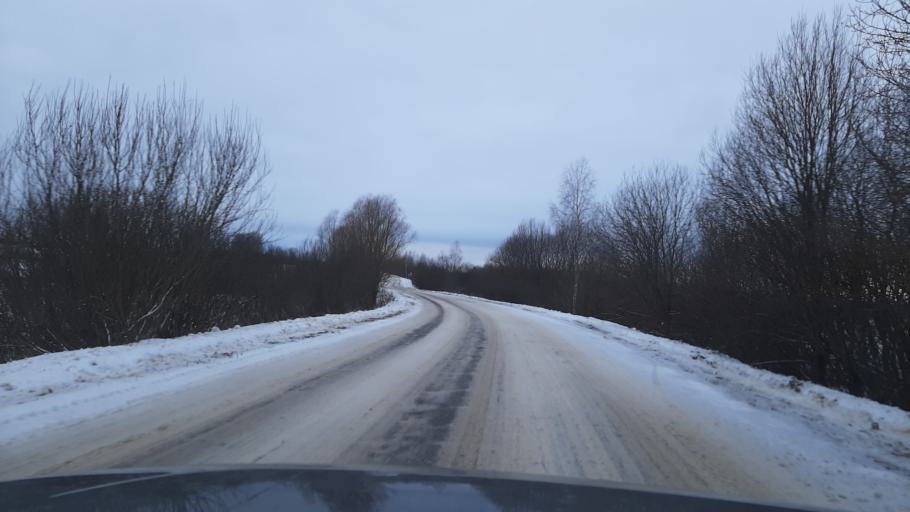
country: RU
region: Kostroma
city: Volgorechensk
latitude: 57.4402
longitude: 41.0994
